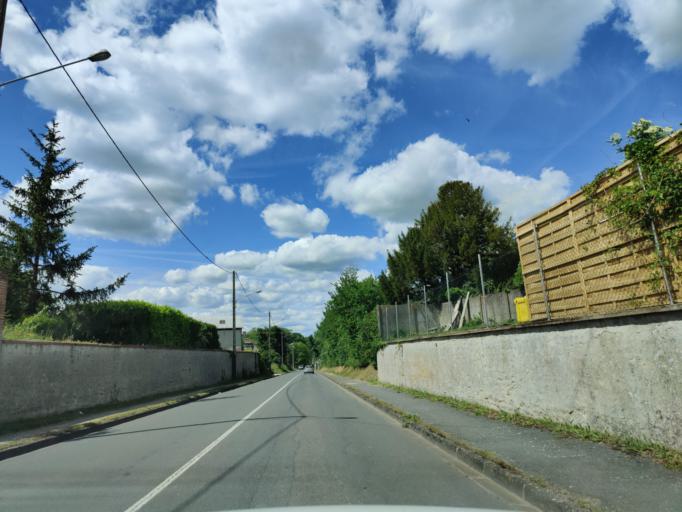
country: FR
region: Centre
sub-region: Departement du Loiret
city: Pithiviers
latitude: 48.1629
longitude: 2.2584
